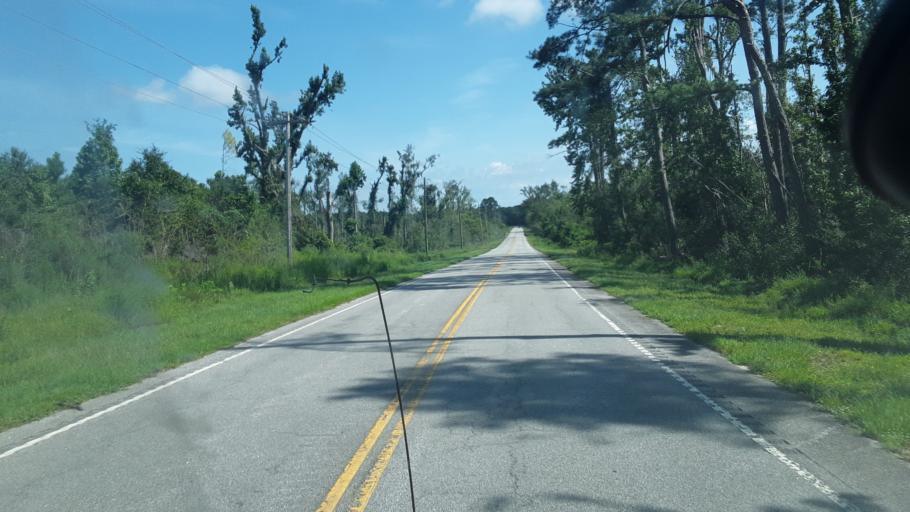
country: US
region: South Carolina
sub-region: Hampton County
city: Varnville
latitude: 32.7933
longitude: -81.0583
